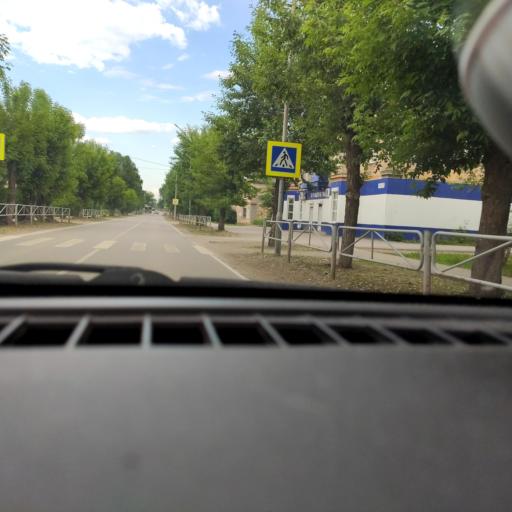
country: RU
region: Perm
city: Krasnokamsk
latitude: 58.0695
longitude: 55.7984
